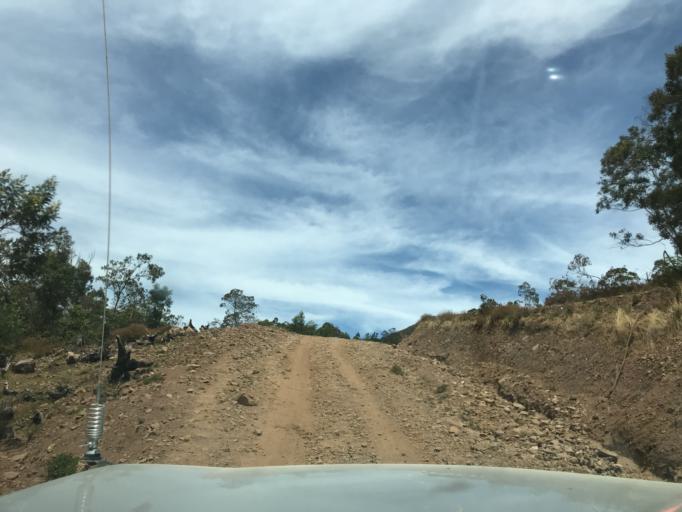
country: TL
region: Ainaro
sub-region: Ainaro
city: Ainaro
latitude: -8.8754
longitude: 125.5295
